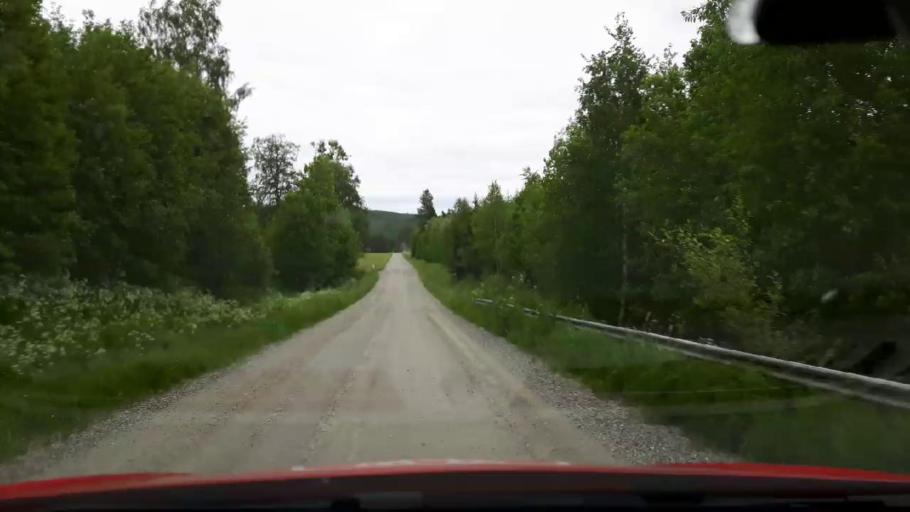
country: SE
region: Jaemtland
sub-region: Ragunda Kommun
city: Hammarstrand
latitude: 63.2121
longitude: 16.0860
